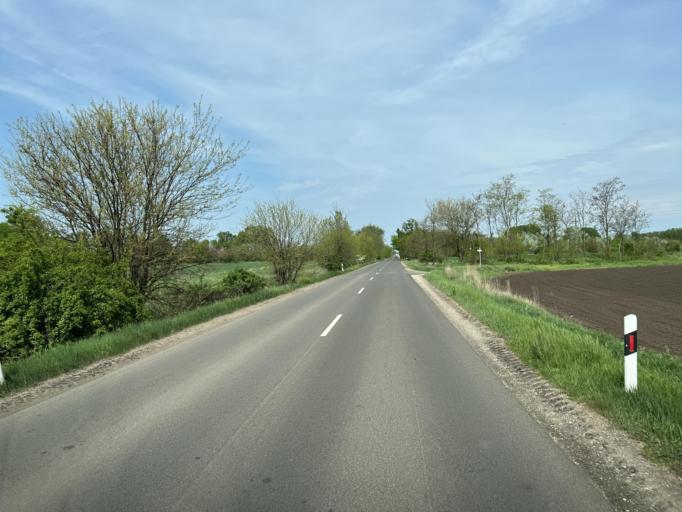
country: HU
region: Pest
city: Abony
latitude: 47.2045
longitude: 19.9919
